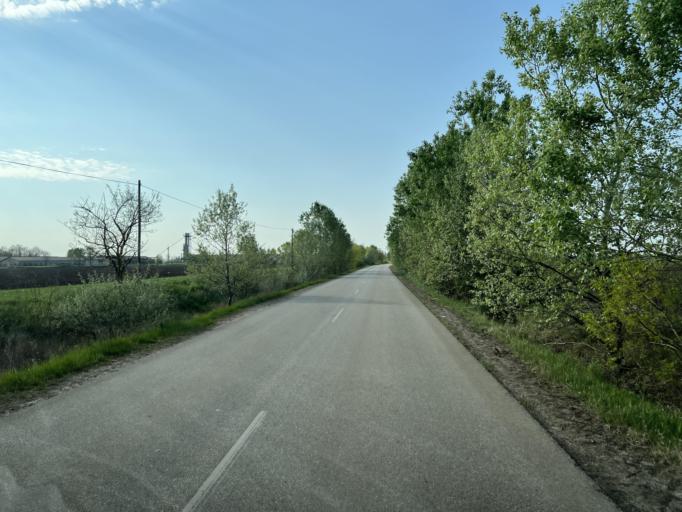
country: HU
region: Pest
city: Jaszkarajeno
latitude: 47.1075
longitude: 20.0179
